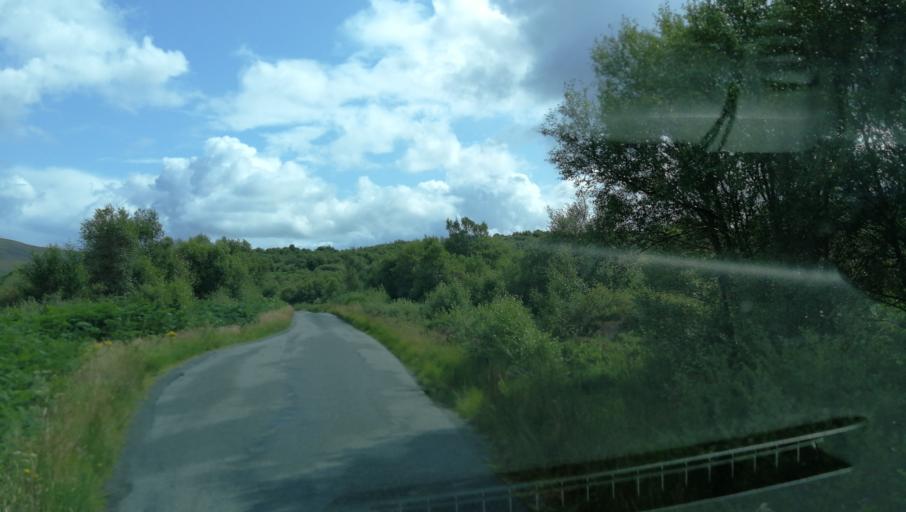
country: GB
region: Scotland
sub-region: Highland
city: Portree
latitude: 57.3836
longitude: -6.1842
